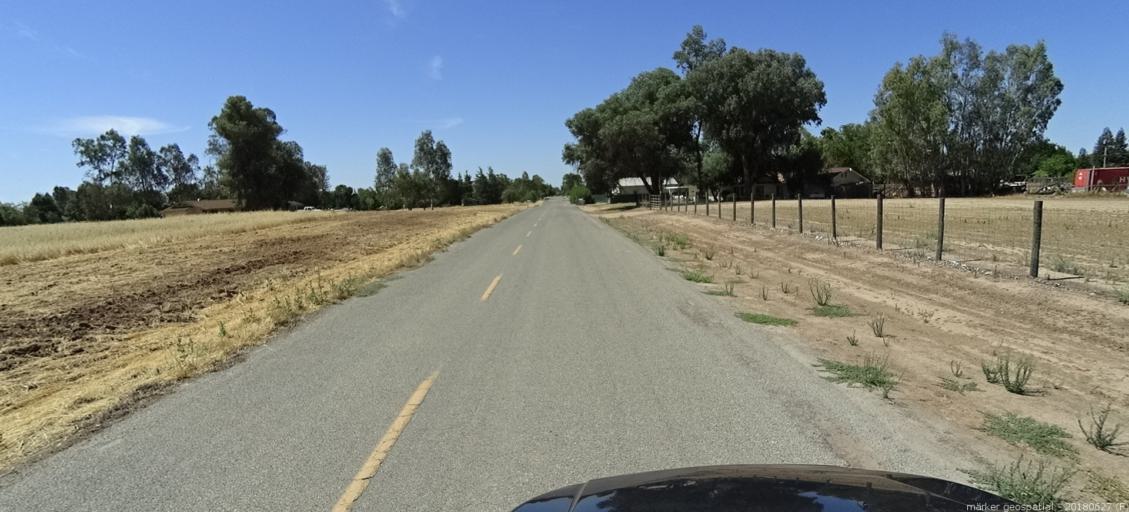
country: US
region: California
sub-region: Madera County
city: Bonadelle Ranchos-Madera Ranchos
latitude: 36.9349
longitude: -119.8795
